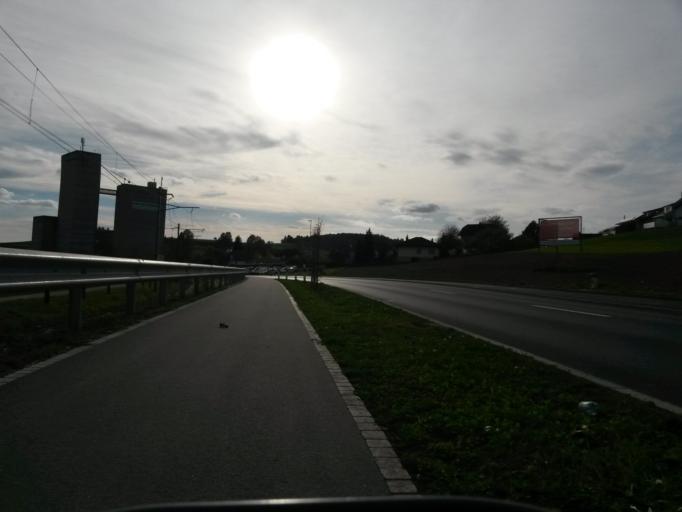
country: CH
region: Bern
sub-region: Emmental District
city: Batterkinden
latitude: 47.1668
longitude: 7.5285
